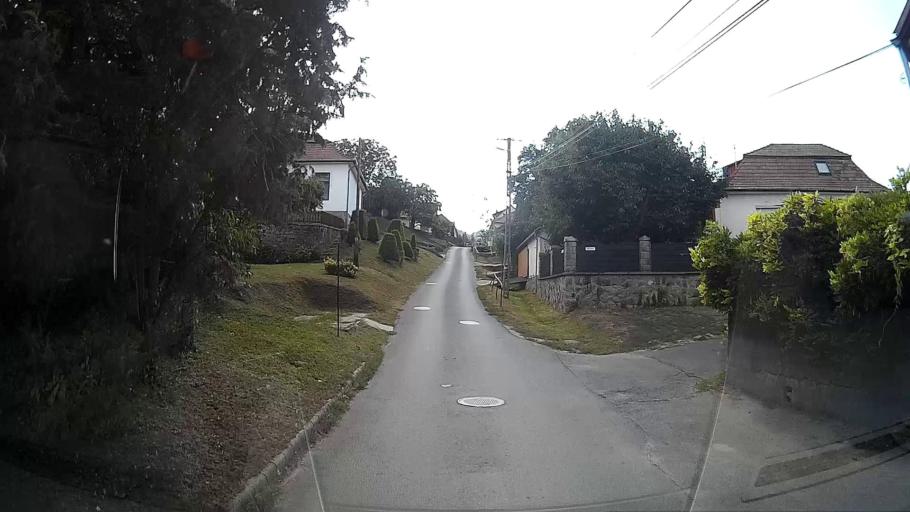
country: HU
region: Pest
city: Dunabogdany
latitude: 47.7927
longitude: 19.0325
